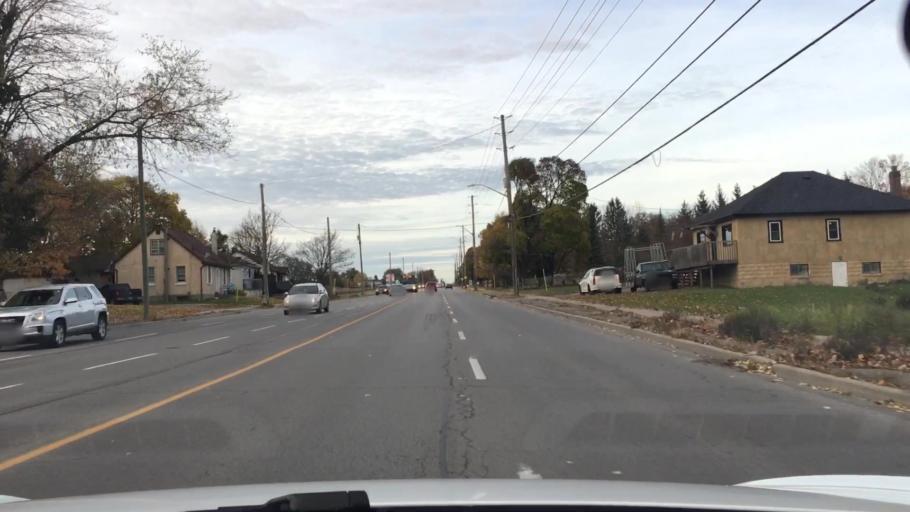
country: CA
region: Ontario
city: Oshawa
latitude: 43.9095
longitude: -78.8146
